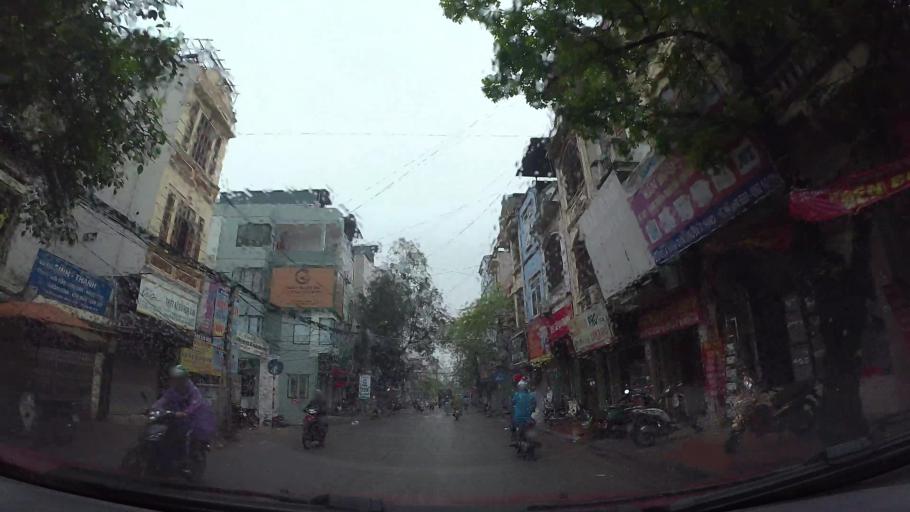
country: VN
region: Ha Noi
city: Dong Da
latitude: 21.0224
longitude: 105.8232
